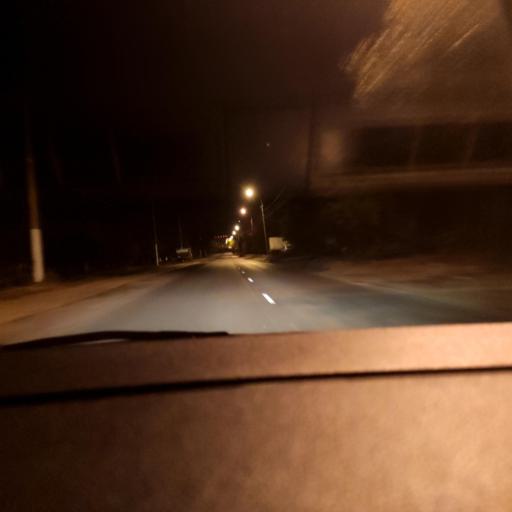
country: RU
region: Voronezj
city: Voronezh
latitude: 51.6979
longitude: 39.1729
